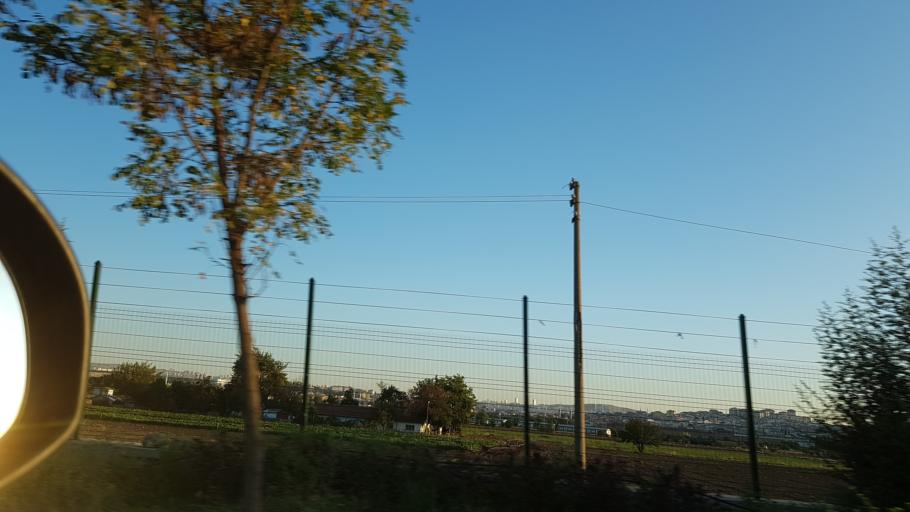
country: TR
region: Ankara
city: Etimesgut
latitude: 39.9626
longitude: 32.6598
